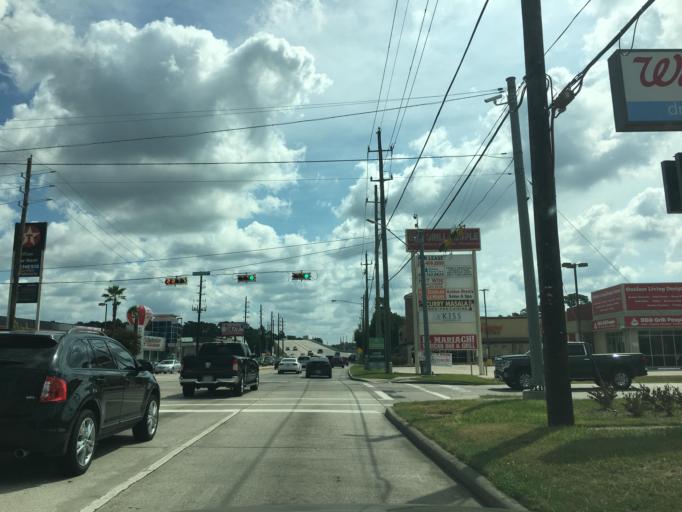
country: US
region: Texas
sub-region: Montgomery County
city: Oak Ridge North
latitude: 30.1273
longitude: -95.4339
